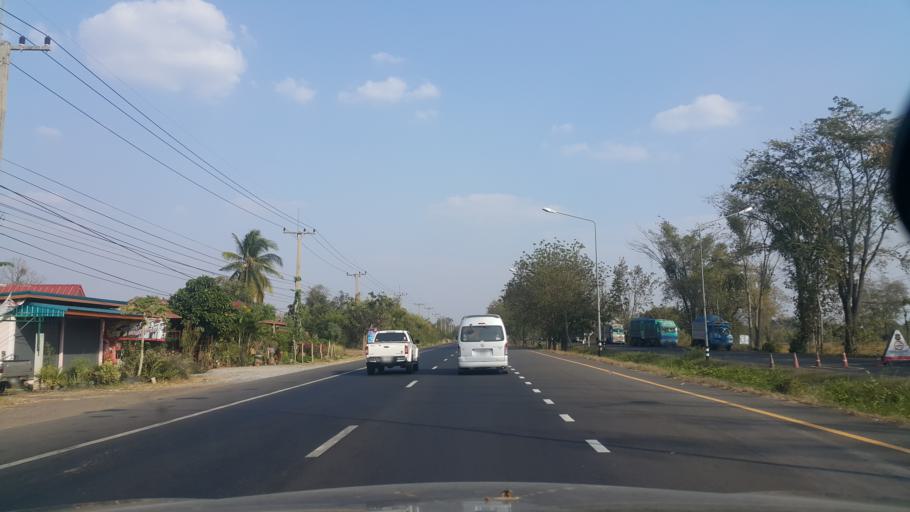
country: TH
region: Buriram
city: Non Suwan
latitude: 14.6556
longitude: 102.6406
